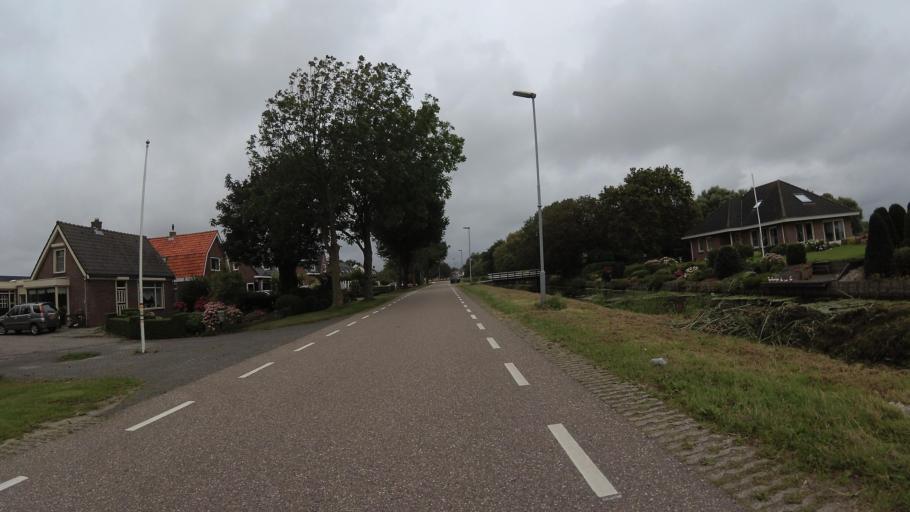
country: NL
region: North Holland
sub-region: Gemeente Den Helder
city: Den Helder
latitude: 52.9279
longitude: 4.7724
